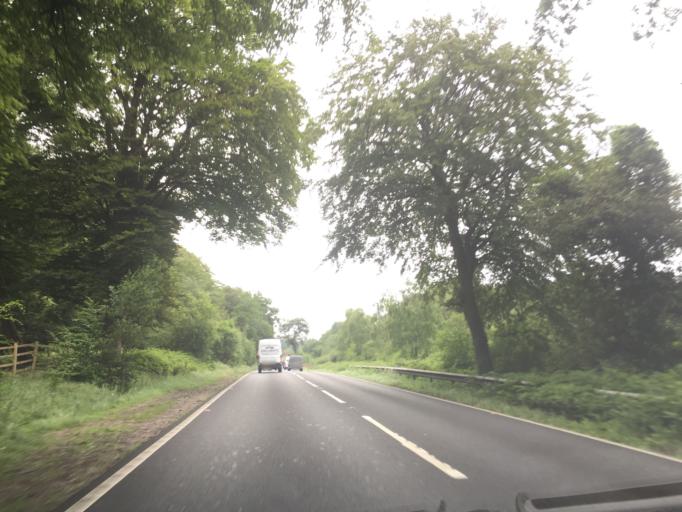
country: GB
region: England
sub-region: Hampshire
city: Cadnam
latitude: 50.9131
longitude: -1.6012
